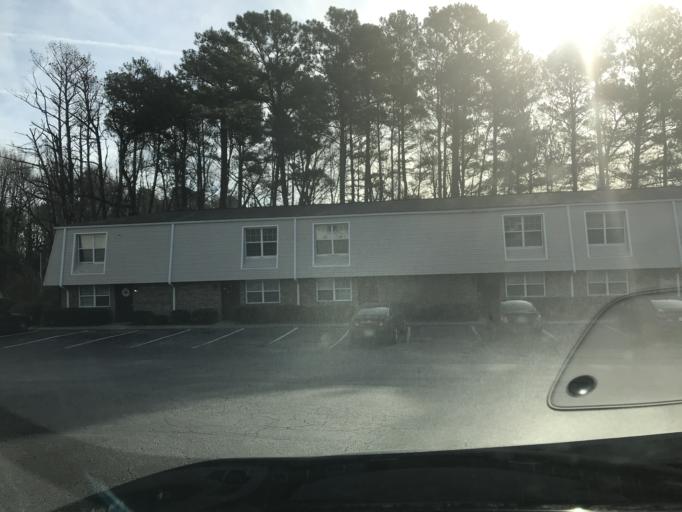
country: US
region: Georgia
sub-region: Clayton County
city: Riverdale
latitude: 33.5789
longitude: -84.3792
